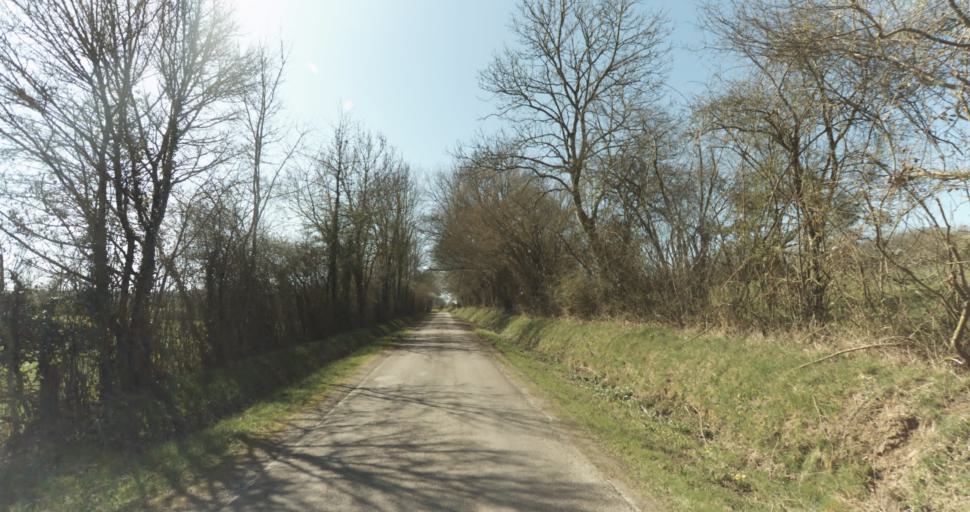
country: FR
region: Lower Normandy
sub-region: Departement du Calvados
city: Livarot
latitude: 48.9993
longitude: 0.0695
